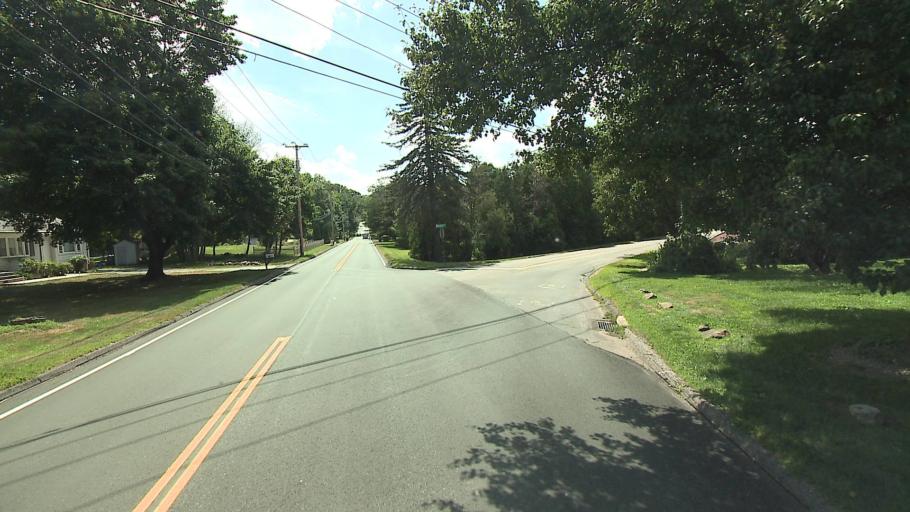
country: US
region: Connecticut
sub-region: Fairfield County
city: Shelton
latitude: 41.2928
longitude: -73.1487
